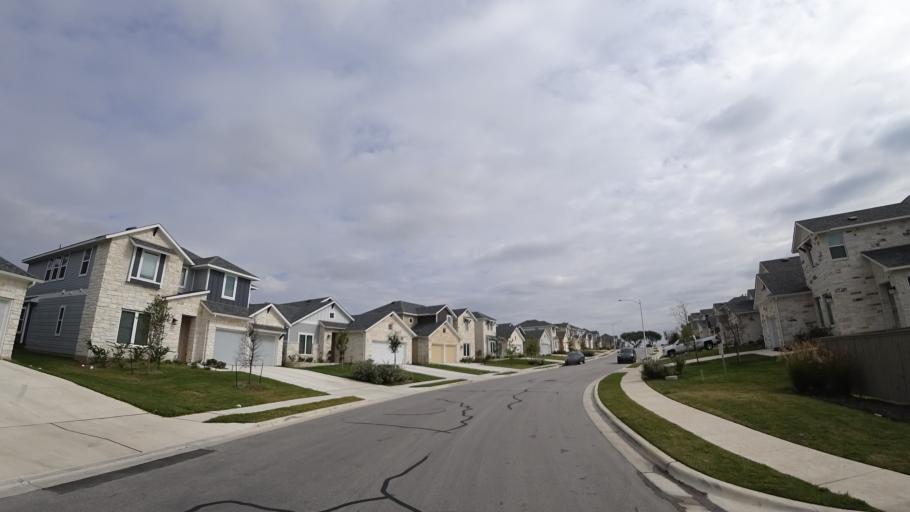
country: US
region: Texas
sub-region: Travis County
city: Wells Branch
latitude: 30.4281
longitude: -97.6993
